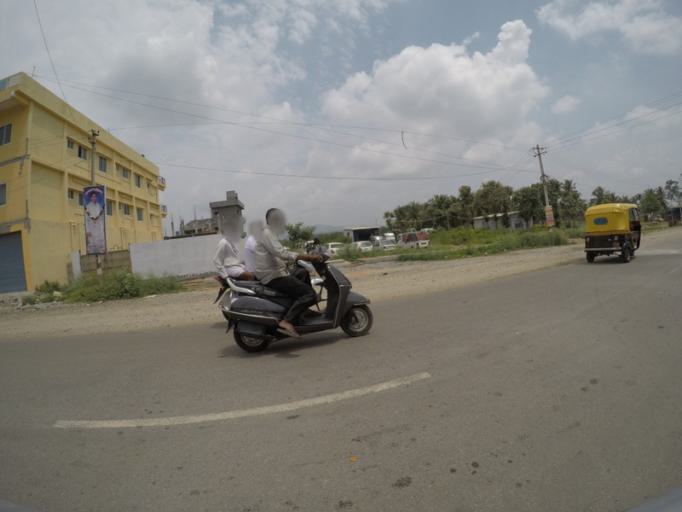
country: IN
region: Karnataka
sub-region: Ramanagara
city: Kanakapura
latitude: 12.5677
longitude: 77.4274
